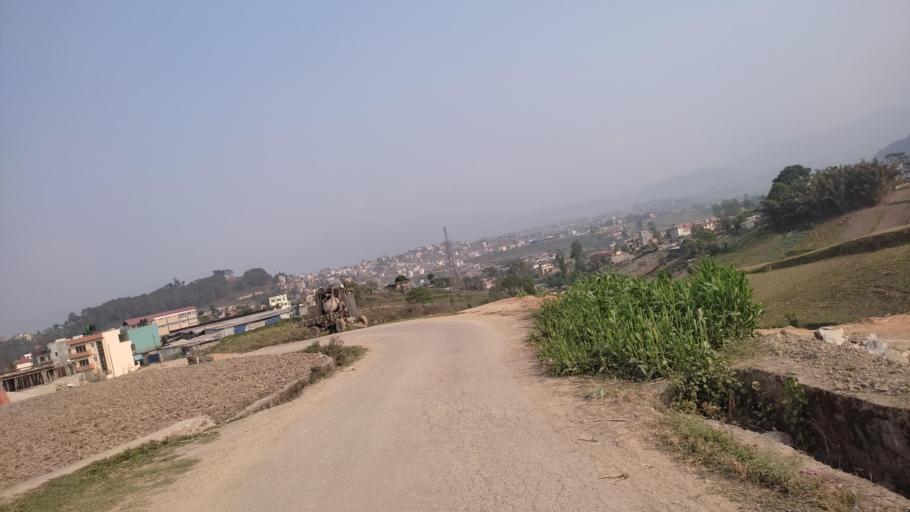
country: NP
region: Central Region
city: Kirtipur
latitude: 27.6602
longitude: 85.2842
